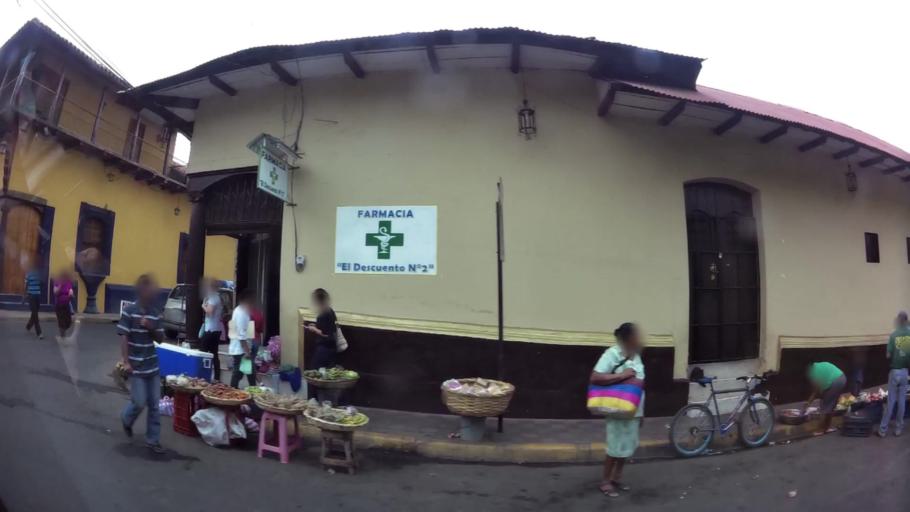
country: NI
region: Leon
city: Leon
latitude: 12.4340
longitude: -86.8774
